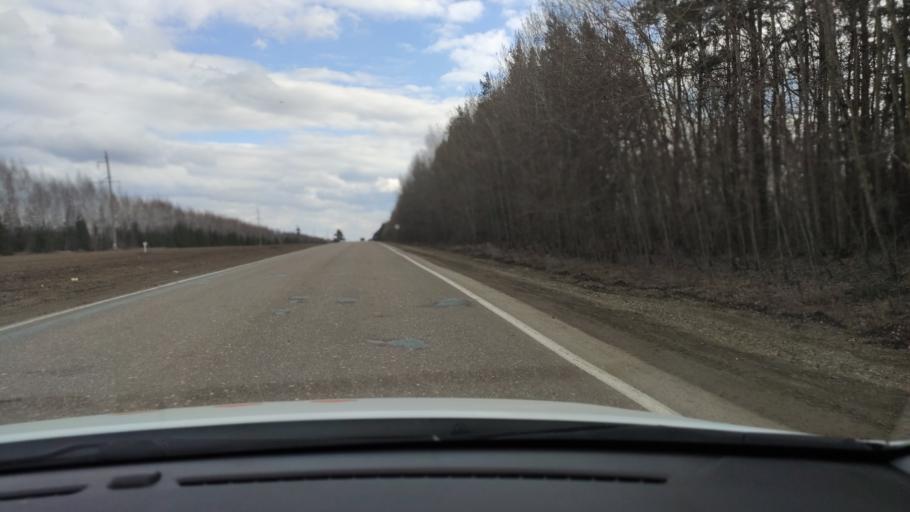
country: RU
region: Tatarstan
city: Vysokaya Gora
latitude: 56.0617
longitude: 49.2043
